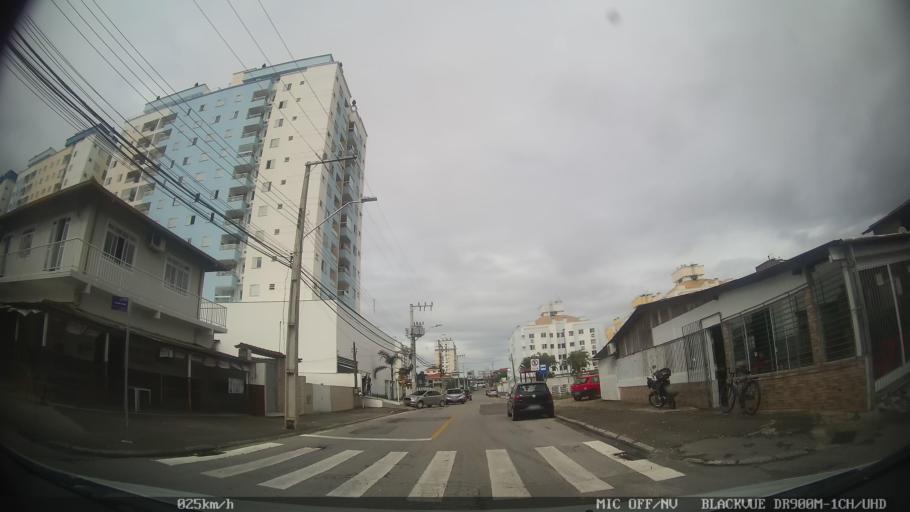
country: BR
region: Santa Catarina
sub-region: Sao Jose
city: Campinas
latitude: -27.5581
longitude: -48.6315
